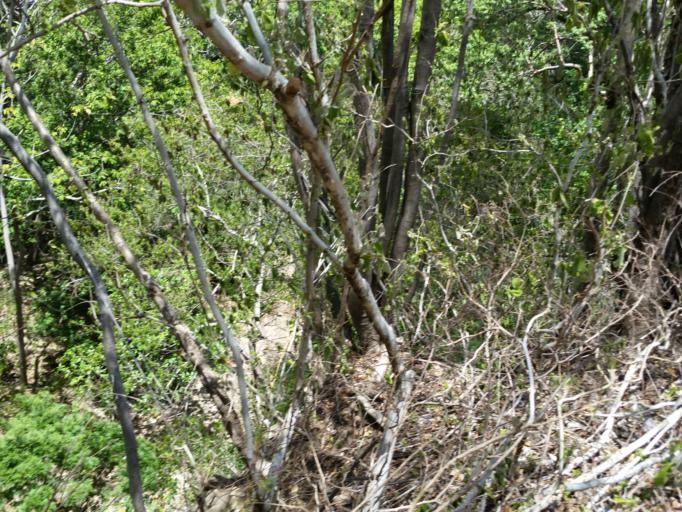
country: NI
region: Managua
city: Carlos Fonseca Amador
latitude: 11.9591
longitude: -86.4304
